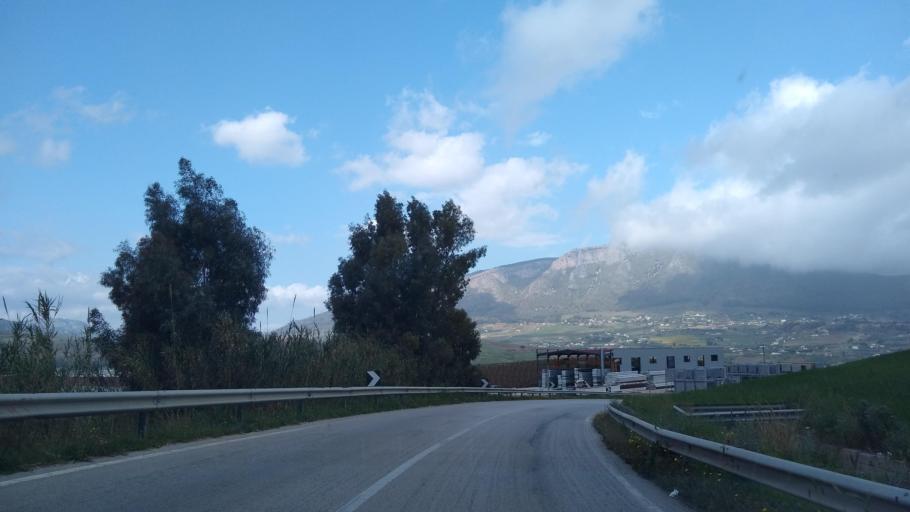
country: IT
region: Sicily
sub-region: Trapani
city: Alcamo
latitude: 37.9706
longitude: 12.9299
